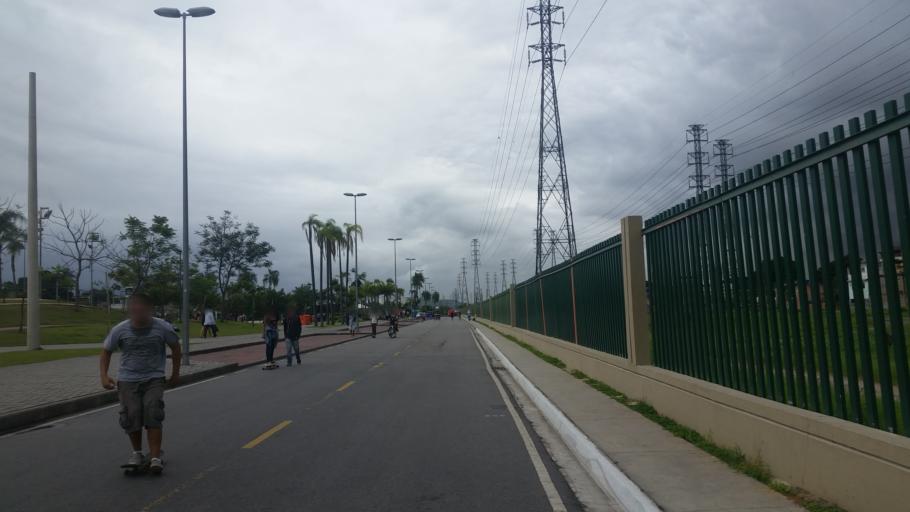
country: BR
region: Rio de Janeiro
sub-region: Sao Joao De Meriti
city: Sao Joao de Meriti
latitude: -22.8643
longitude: -43.3443
